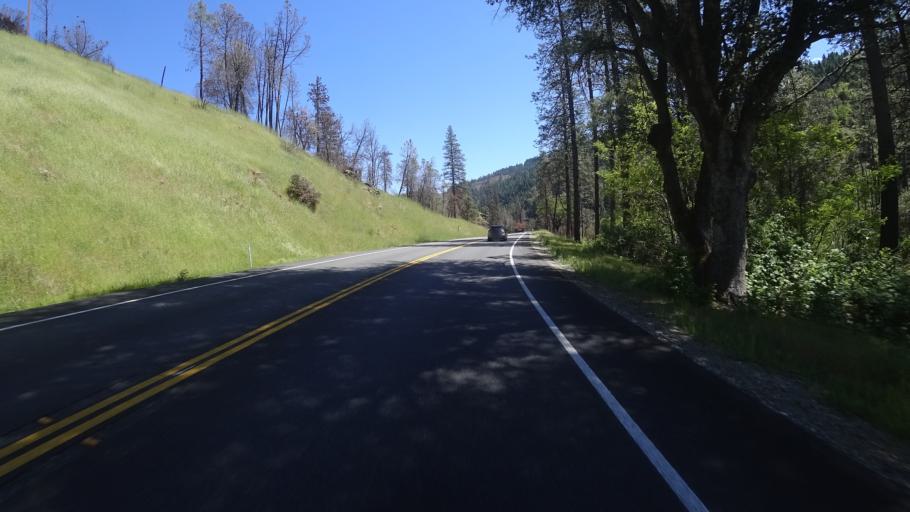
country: US
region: California
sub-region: Trinity County
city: Weaverville
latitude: 40.7709
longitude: -123.1250
